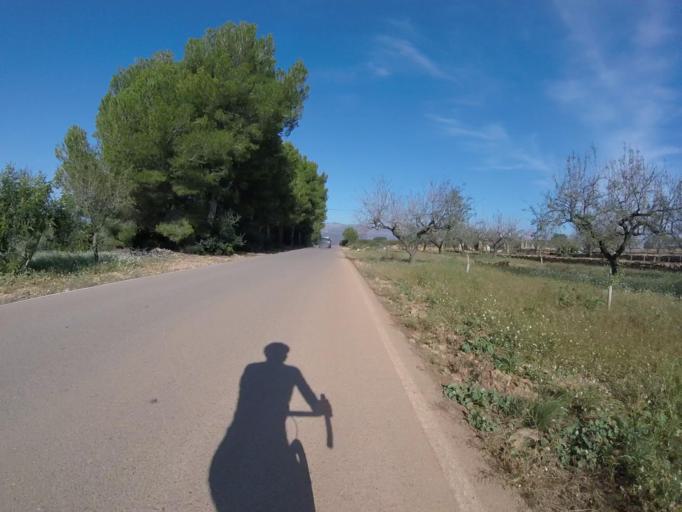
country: ES
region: Valencia
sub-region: Provincia de Castello
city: Benlloch
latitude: 40.2372
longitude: 0.0733
